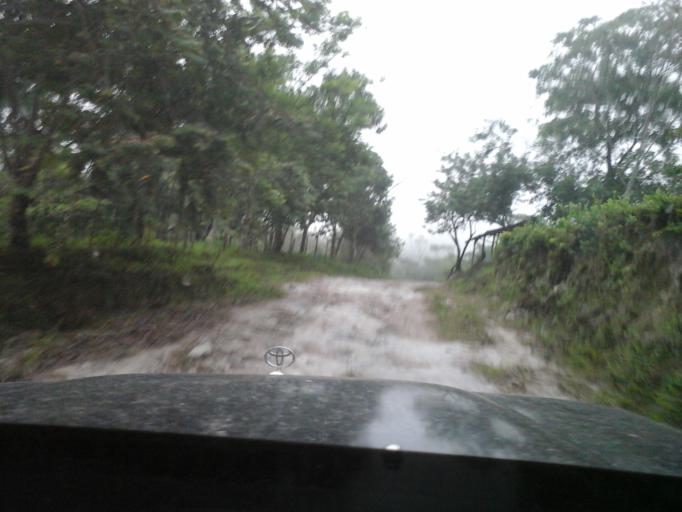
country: CO
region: Cesar
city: Agustin Codazzi
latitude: 9.9391
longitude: -73.1455
